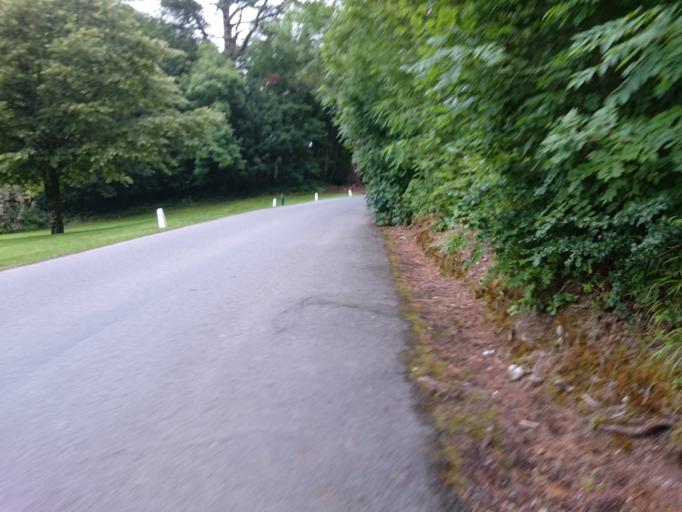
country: IE
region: Connaught
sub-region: Maigh Eo
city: Ballinrobe
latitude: 53.5382
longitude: -9.2858
